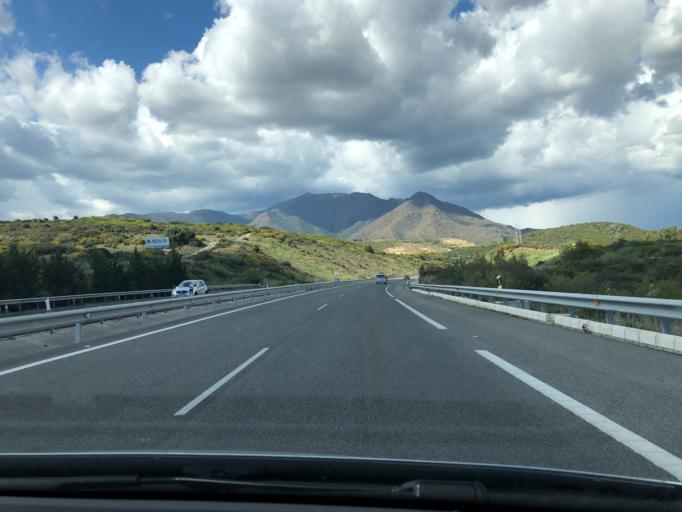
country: ES
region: Andalusia
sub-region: Provincia de Malaga
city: Manilva
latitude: 36.4169
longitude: -5.2206
